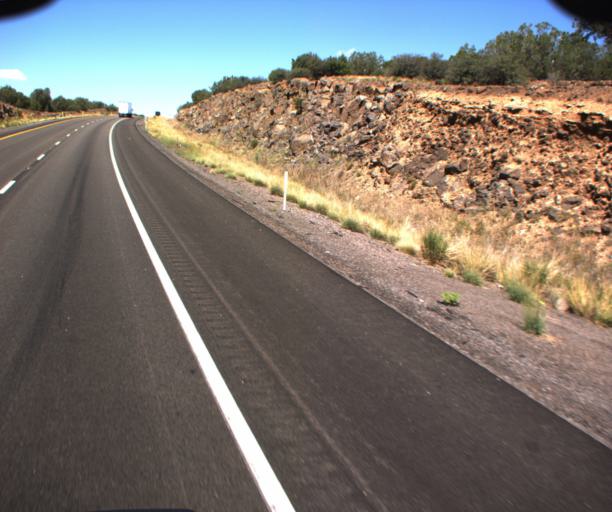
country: US
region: Arizona
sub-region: Mohave County
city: Peach Springs
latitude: 35.1898
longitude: -113.3215
